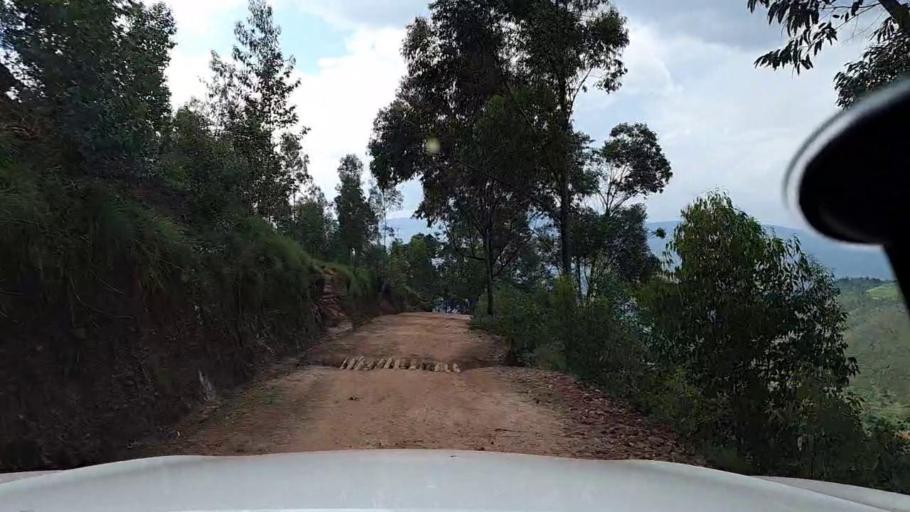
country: RW
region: Southern Province
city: Gitarama
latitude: -1.8391
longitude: 29.8258
